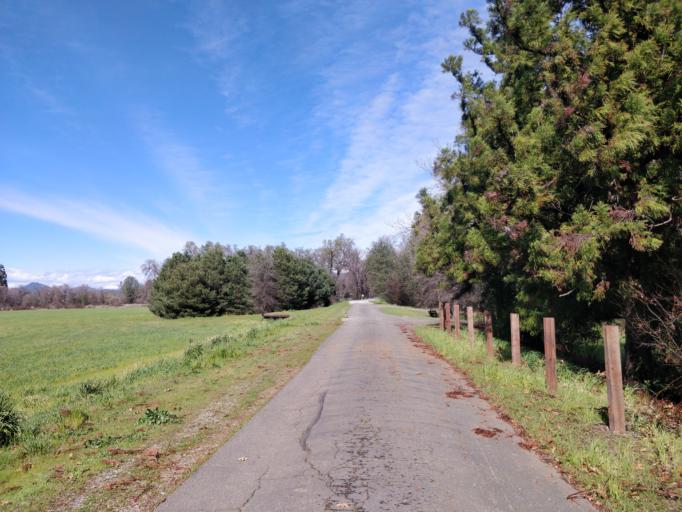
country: US
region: California
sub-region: Shasta County
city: Shasta Lake
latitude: 40.6275
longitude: -122.3127
